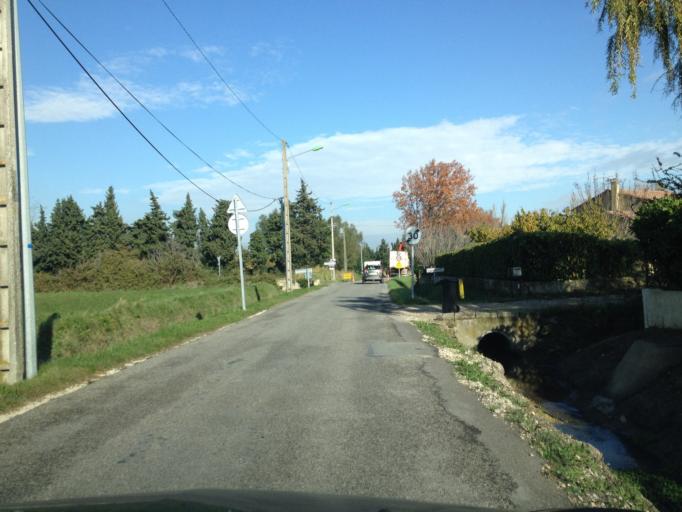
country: FR
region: Provence-Alpes-Cote d'Azur
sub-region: Departement du Vaucluse
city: Bedarrides
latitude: 44.0480
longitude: 4.9007
